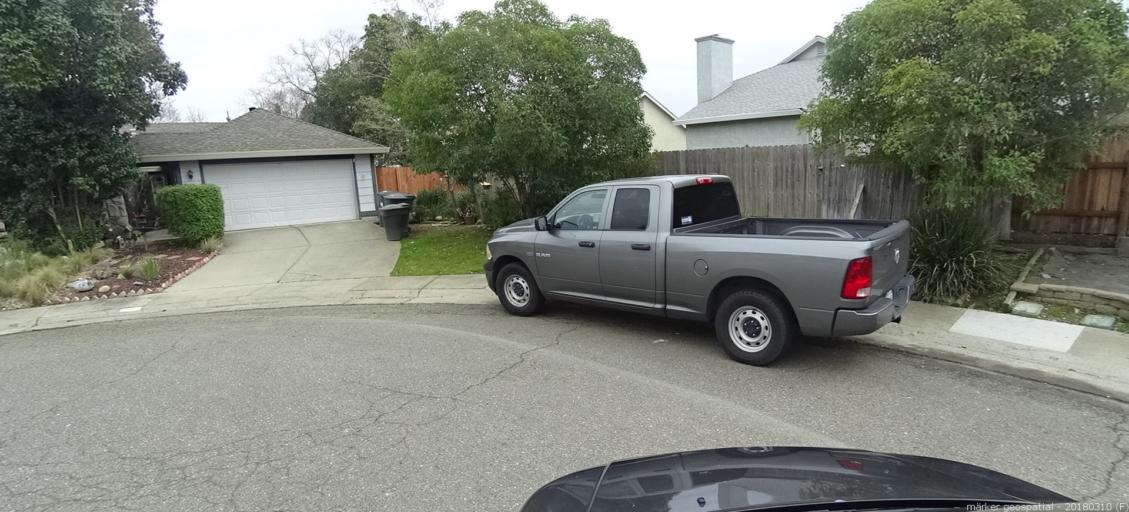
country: US
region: California
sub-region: Sacramento County
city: Vineyard
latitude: 38.4648
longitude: -121.3751
